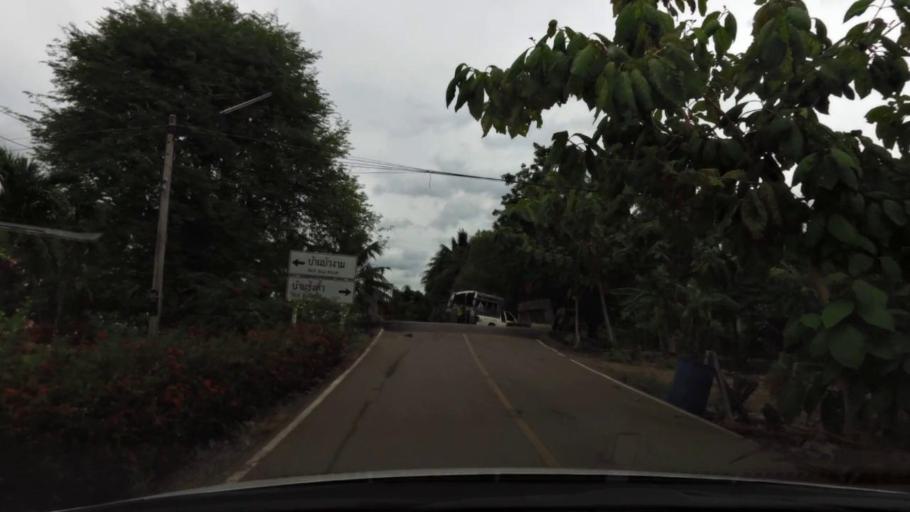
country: TH
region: Samut Sakhon
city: Ban Phaeo
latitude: 13.5603
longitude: 100.0340
